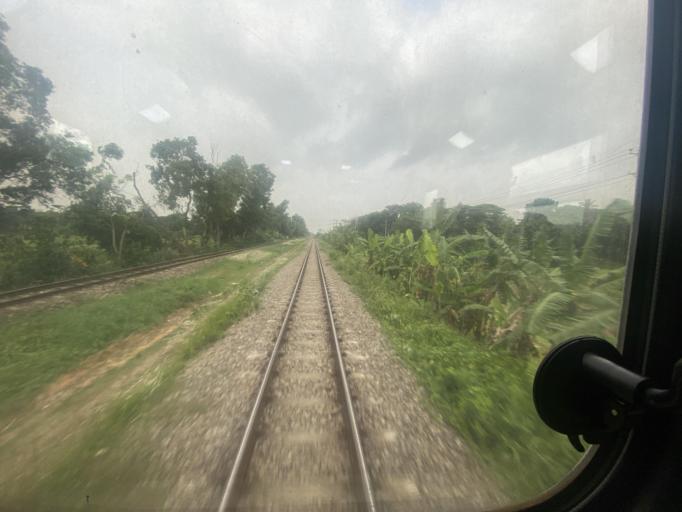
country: BD
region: Dhaka
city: Tungi
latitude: 23.9328
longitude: 90.5126
